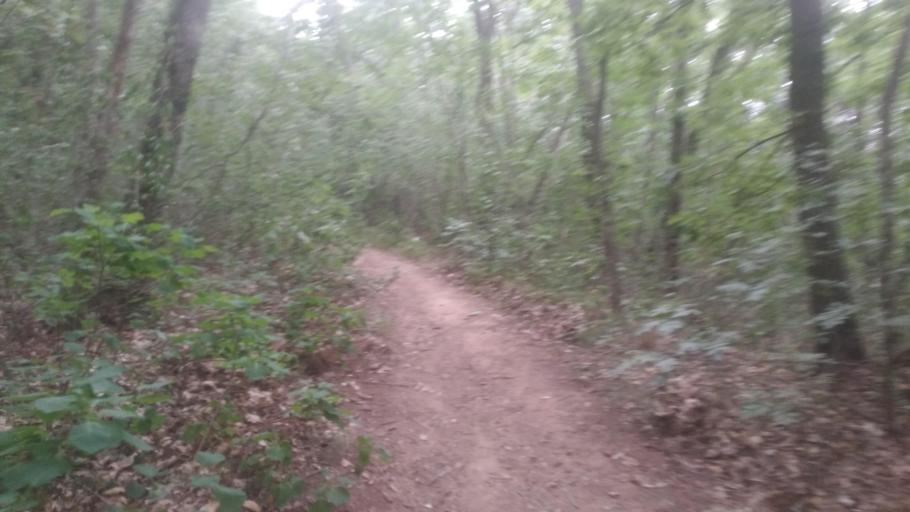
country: HU
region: Veszprem
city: Szentkiralyszabadja
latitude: 47.0075
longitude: 17.9779
